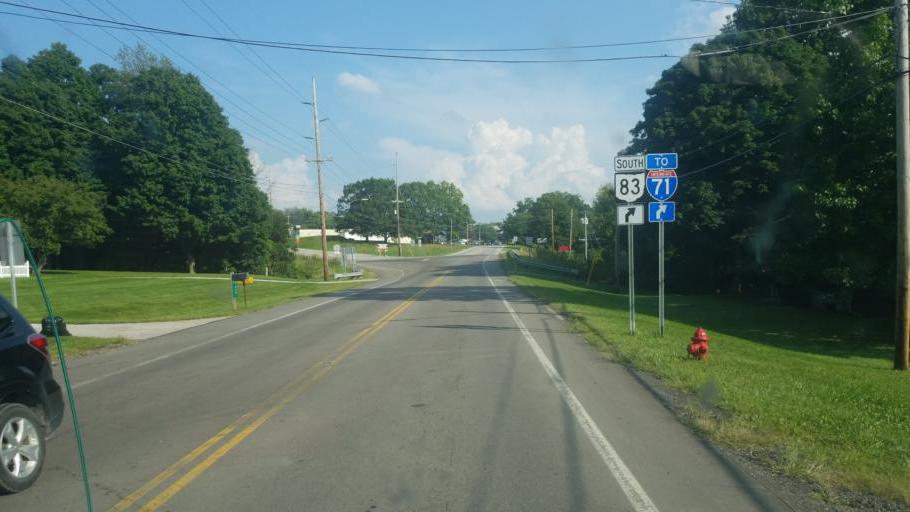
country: US
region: Ohio
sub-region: Medina County
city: Lodi
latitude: 41.0270
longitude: -81.9997
